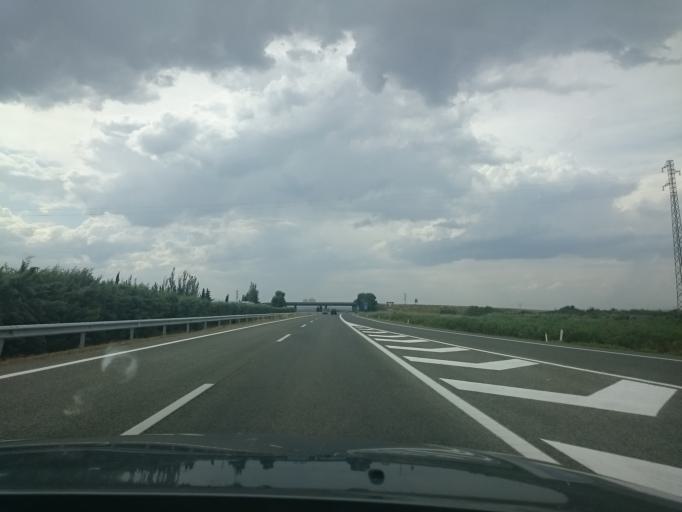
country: ES
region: Navarre
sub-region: Provincia de Navarra
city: Corella
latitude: 42.1351
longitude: -1.7720
